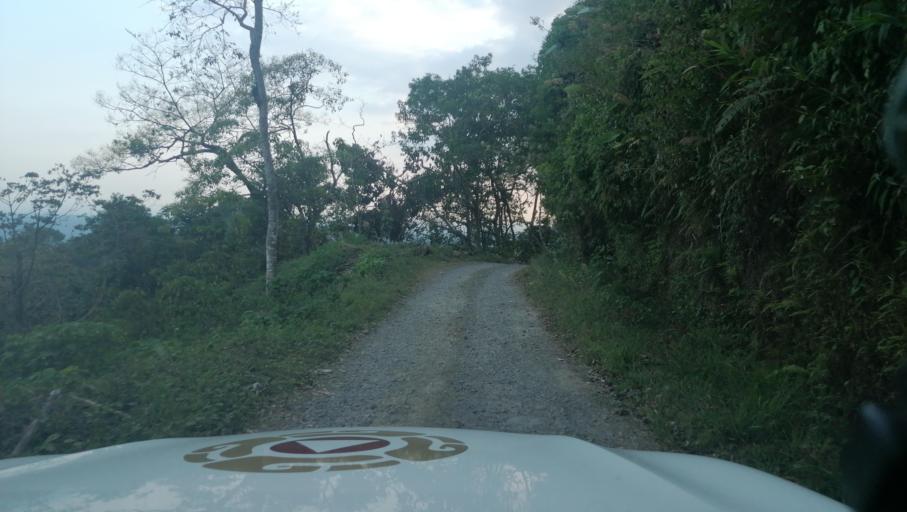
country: MX
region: Chiapas
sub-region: Cacahoatan
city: Benito Juarez
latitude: 15.0960
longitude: -92.2206
